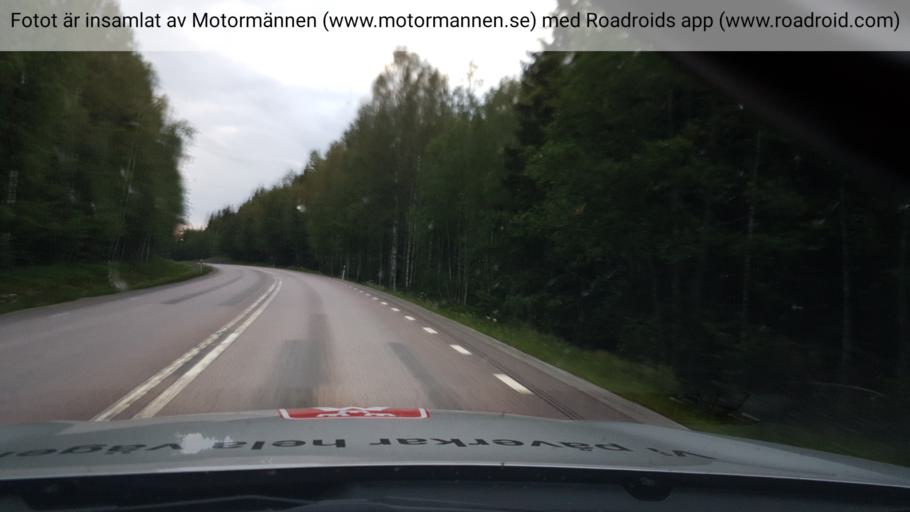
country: SE
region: Vaestmanland
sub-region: Skinnskattebergs Kommun
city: Skinnskatteberg
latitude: 59.9056
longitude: 15.7225
